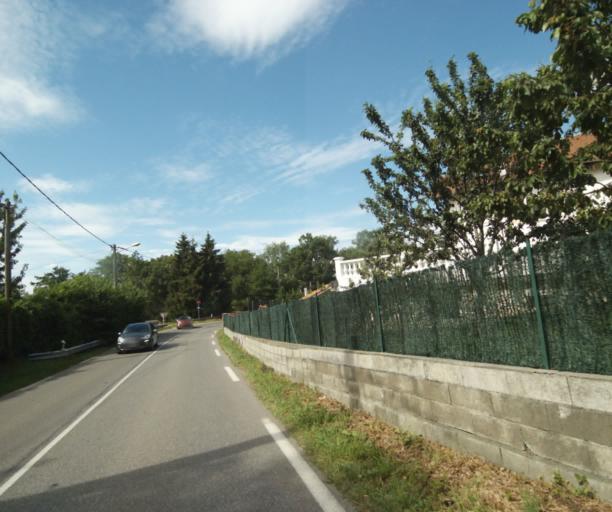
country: FR
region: Rhone-Alpes
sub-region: Departement de la Haute-Savoie
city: Thonon-les-Bains
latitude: 46.3561
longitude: 6.4760
